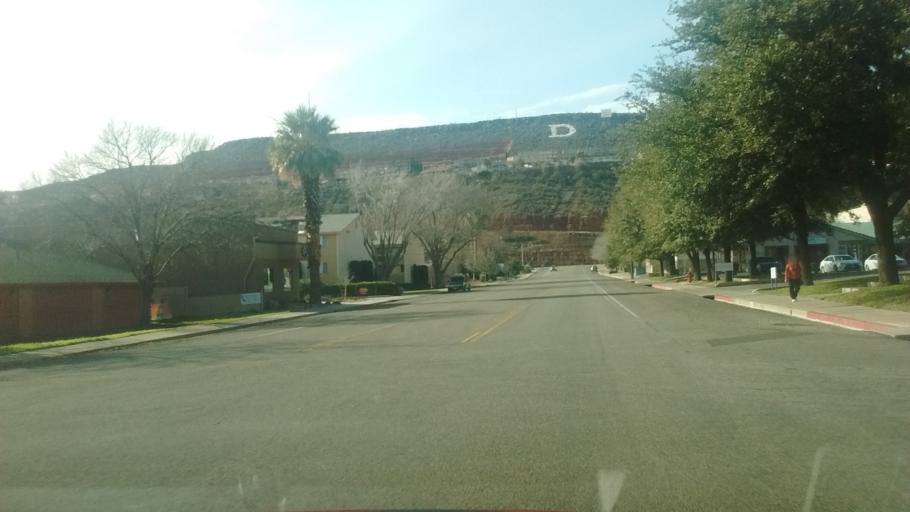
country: US
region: Utah
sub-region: Washington County
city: Saint George
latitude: 37.1083
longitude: -113.5896
